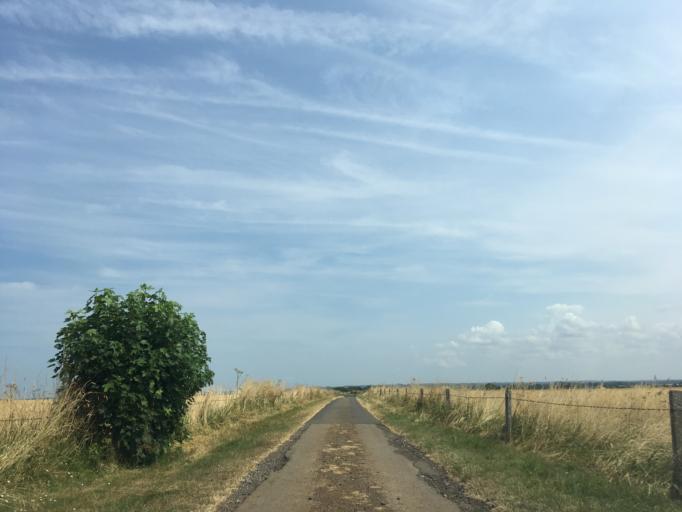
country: GB
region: England
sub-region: Gloucestershire
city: Nailsworth
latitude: 51.6631
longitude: -2.2423
